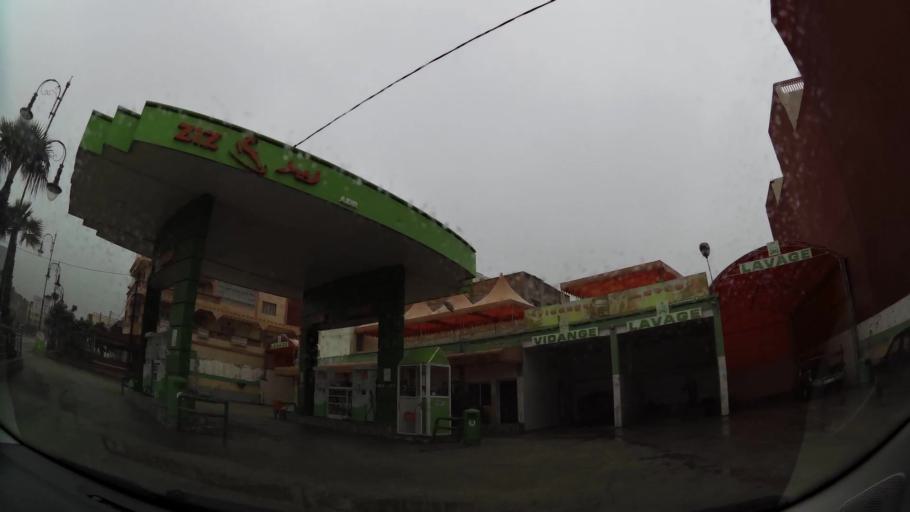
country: MA
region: Taza-Al Hoceima-Taounate
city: Tirhanimine
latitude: 35.1941
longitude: -3.9097
